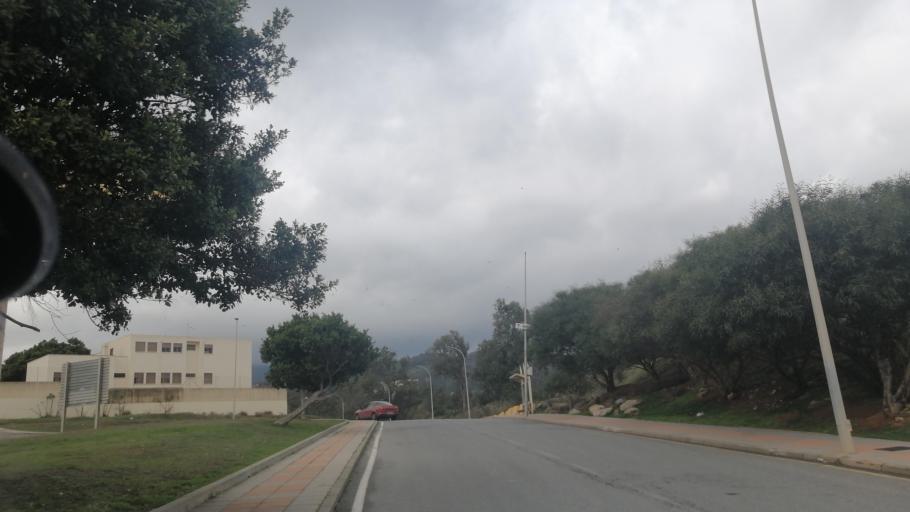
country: ES
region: Ceuta
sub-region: Ceuta
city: Ceuta
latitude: 35.8816
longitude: -5.3442
